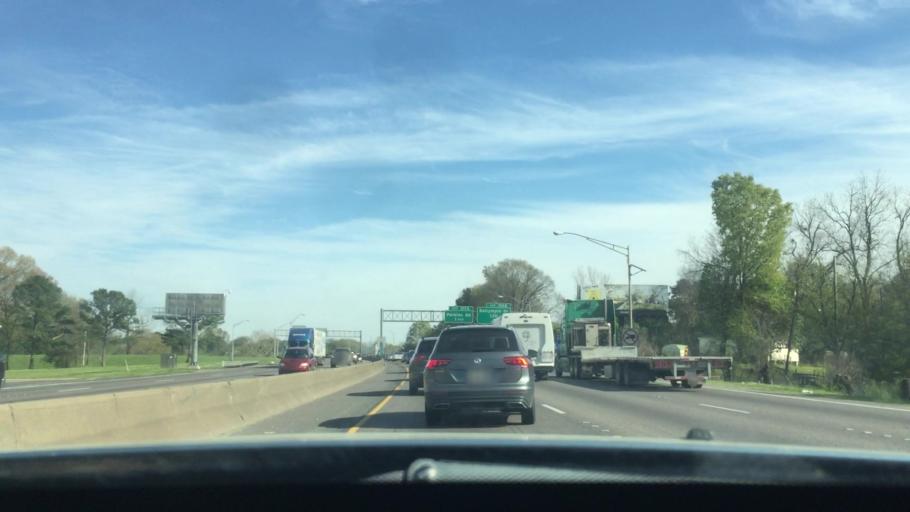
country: US
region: Louisiana
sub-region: East Baton Rouge Parish
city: Baton Rouge
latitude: 30.4290
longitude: -91.1720
